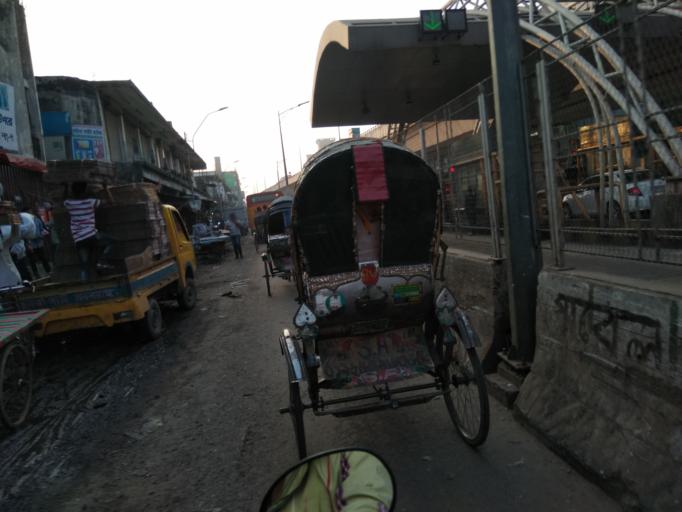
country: BD
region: Dhaka
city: Paltan
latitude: 23.7228
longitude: 90.4137
